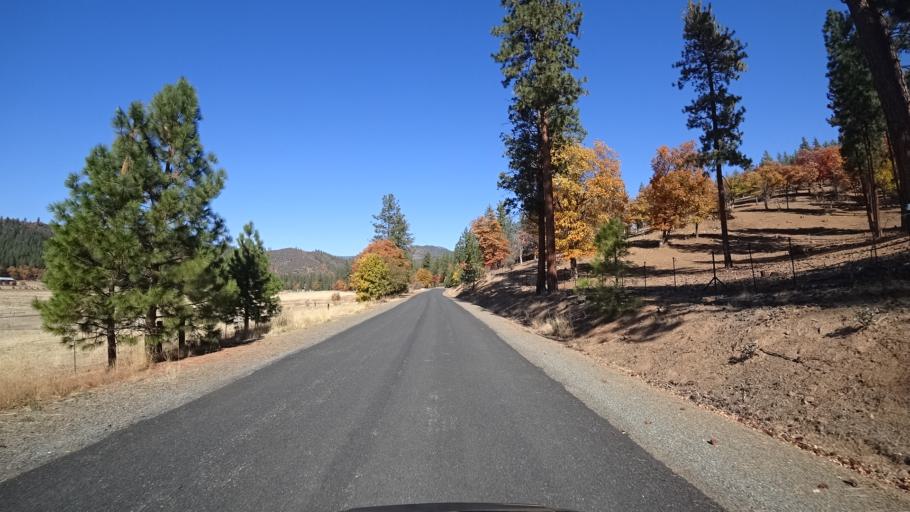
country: US
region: California
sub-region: Siskiyou County
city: Yreka
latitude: 41.6347
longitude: -122.8734
